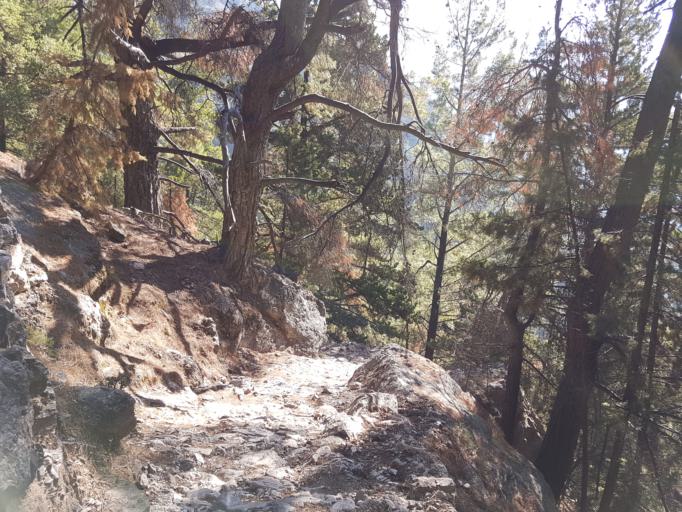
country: GR
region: Crete
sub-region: Nomos Chanias
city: Perivolia
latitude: 35.3091
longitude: 23.9247
